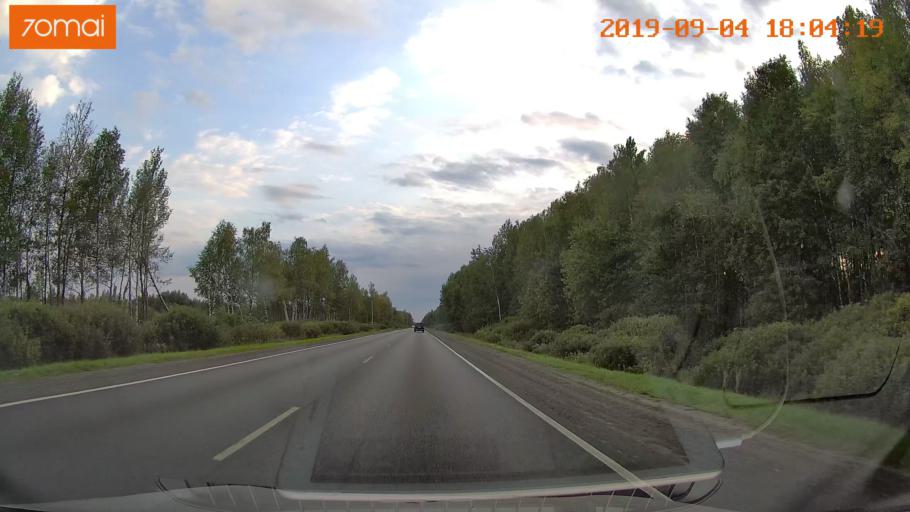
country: RU
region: Moskovskaya
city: Il'inskiy Pogost
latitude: 55.4537
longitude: 38.8408
